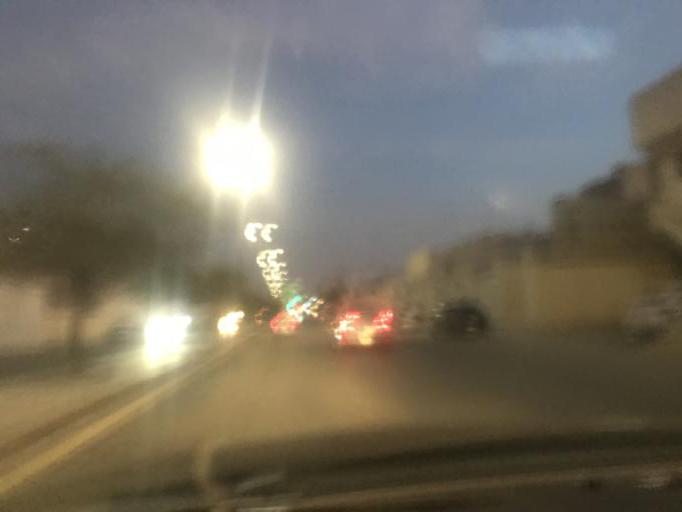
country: SA
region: Ar Riyad
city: Riyadh
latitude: 24.7339
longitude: 46.7600
